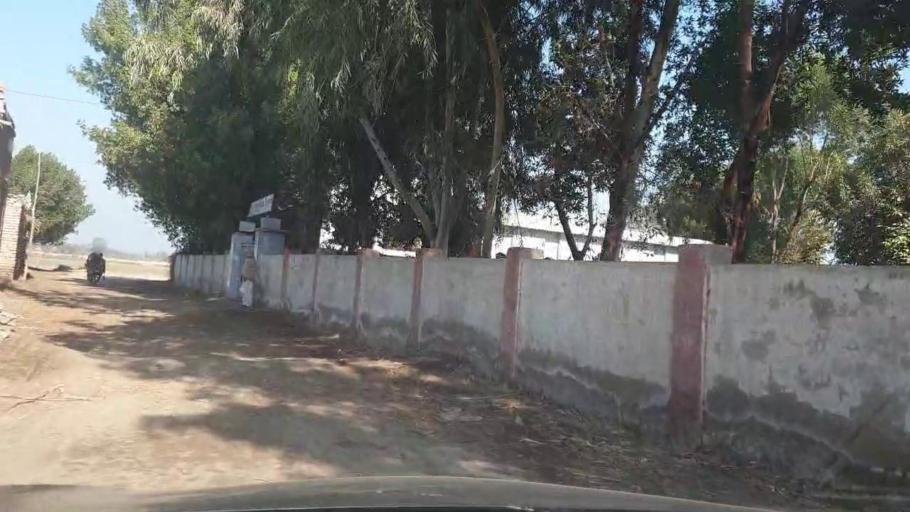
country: PK
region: Sindh
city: Ubauro
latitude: 28.1453
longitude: 69.6975
